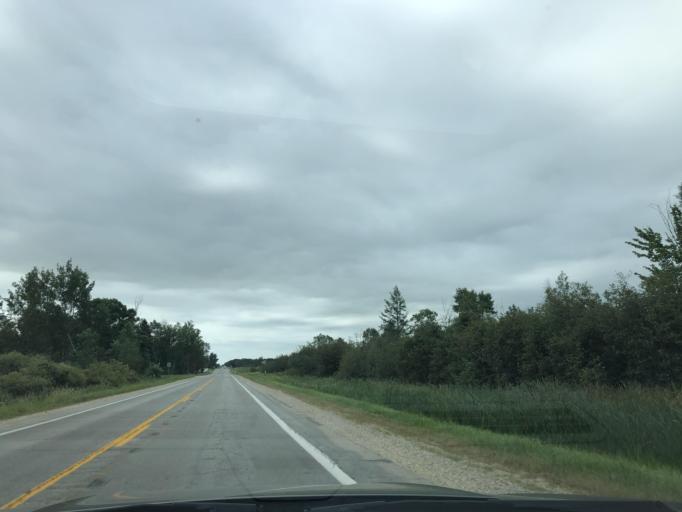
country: US
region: Michigan
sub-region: Missaukee County
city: Lake City
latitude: 44.2282
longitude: -85.2148
